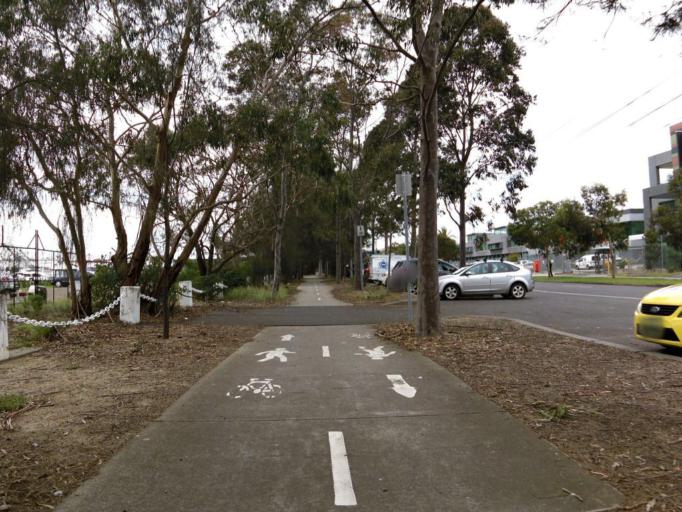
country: AU
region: Victoria
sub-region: Maribyrnong
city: Yarraville
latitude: -37.8255
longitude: 144.9048
